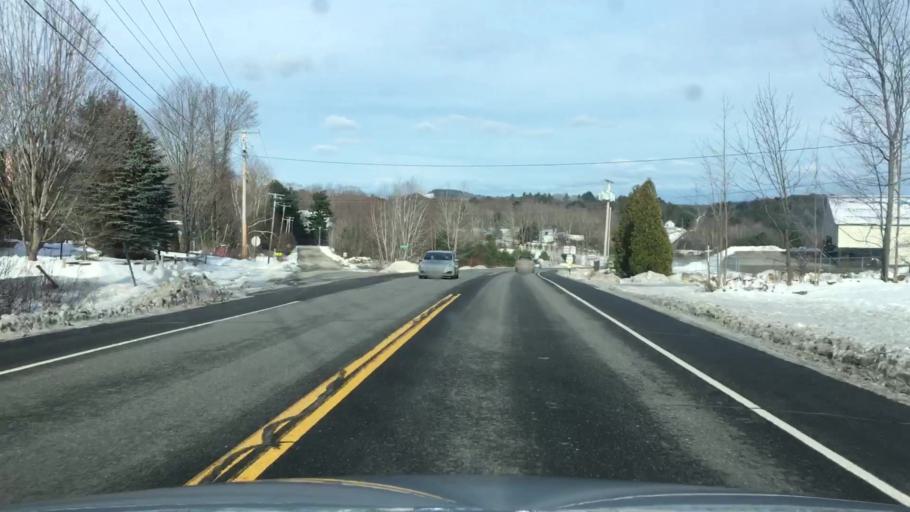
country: US
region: Maine
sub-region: Androscoggin County
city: Greene
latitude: 44.1603
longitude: -70.1841
